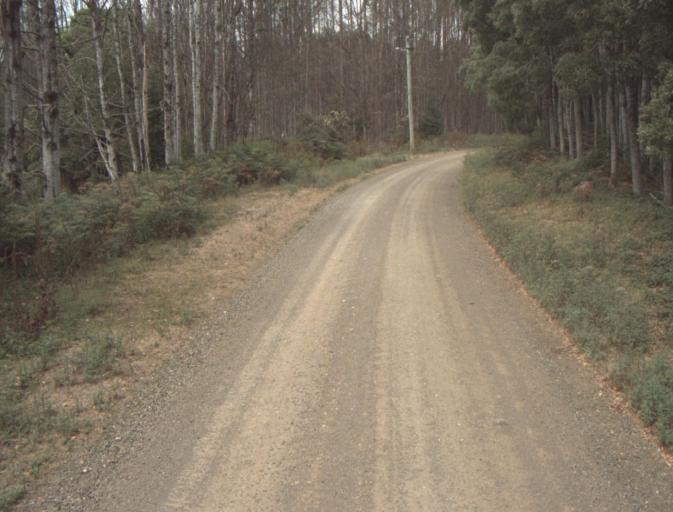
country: AU
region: Tasmania
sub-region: Launceston
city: Mayfield
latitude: -41.1999
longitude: 147.2622
